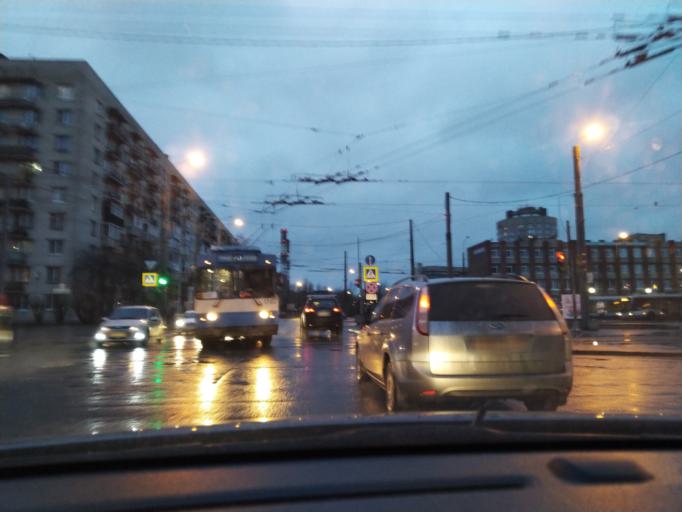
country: RU
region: St.-Petersburg
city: Uritsk
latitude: 59.8331
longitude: 30.1824
